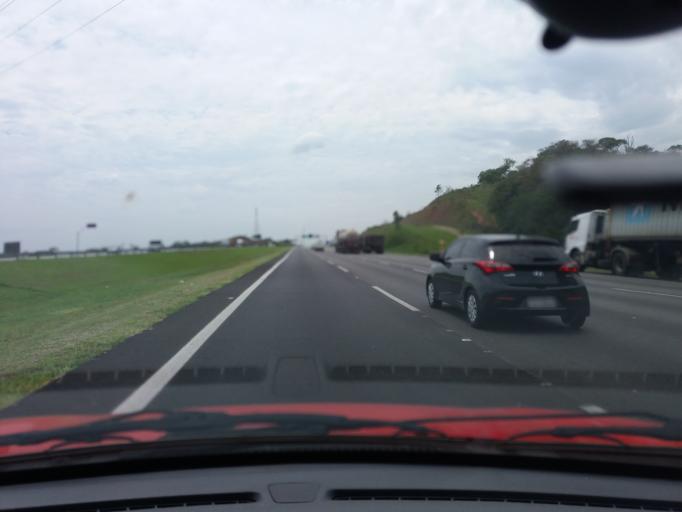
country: BR
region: Sao Paulo
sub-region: Osasco
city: Osasco
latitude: -23.4470
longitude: -46.7805
